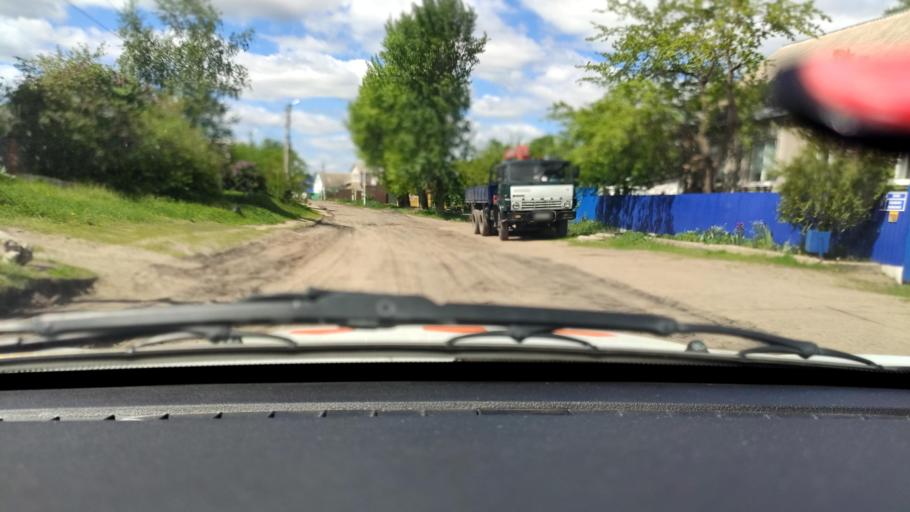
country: RU
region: Voronezj
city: Podgornoye
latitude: 51.7356
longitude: 39.1539
